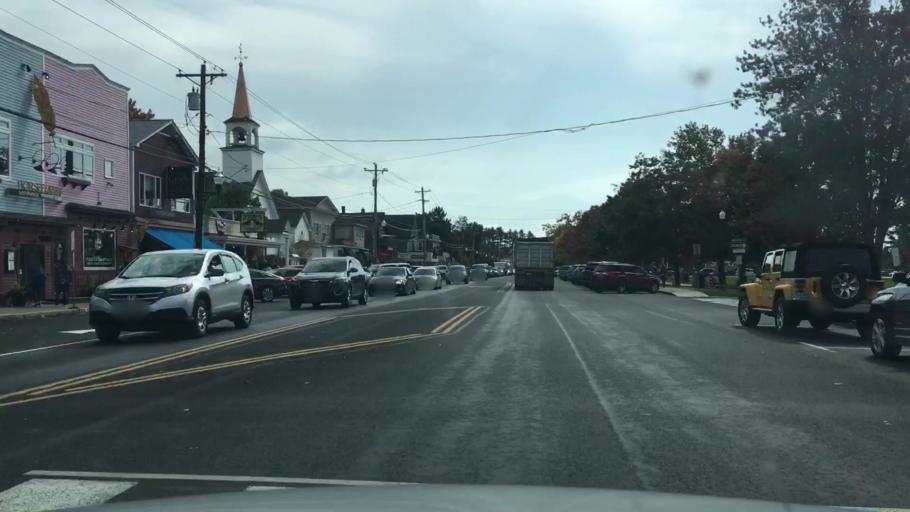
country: US
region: New Hampshire
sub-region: Carroll County
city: North Conway
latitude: 44.0529
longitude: -71.1279
